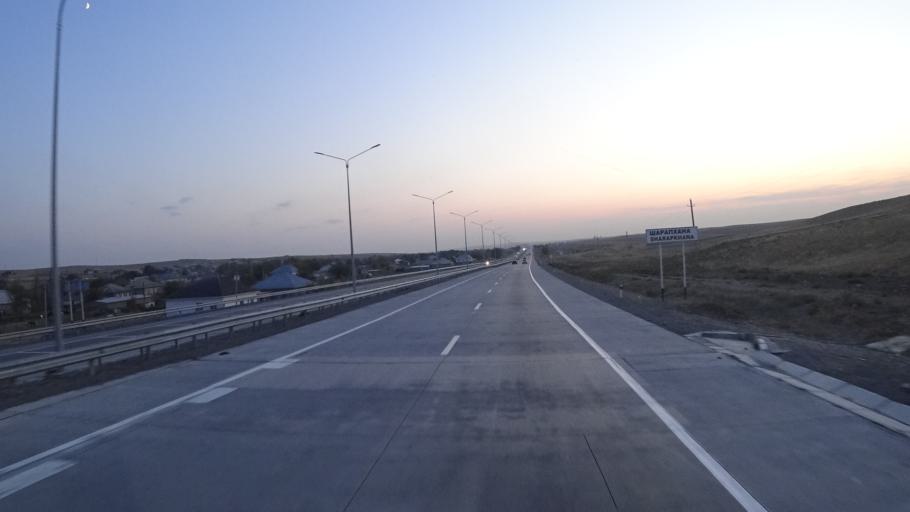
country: KZ
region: Ongtustik Qazaqstan
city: Qazyqurt
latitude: 41.8951
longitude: 69.4520
